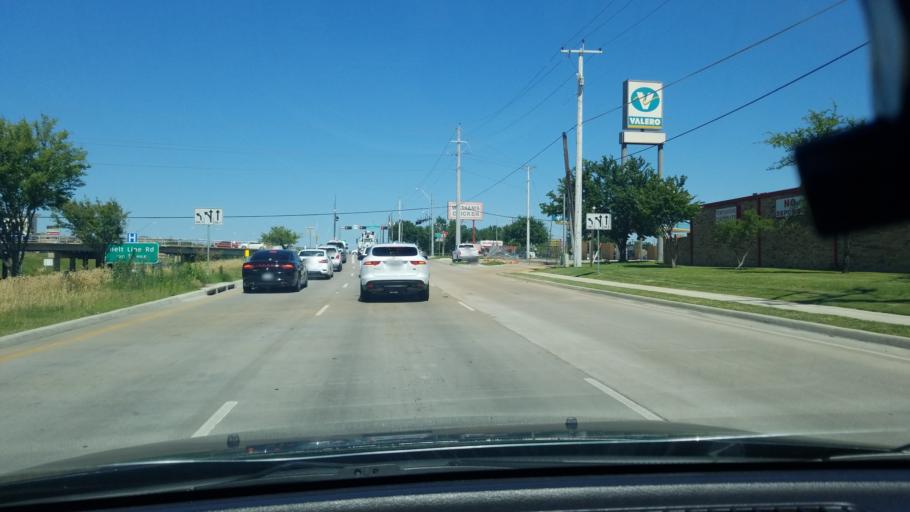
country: US
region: Texas
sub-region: Dallas County
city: Mesquite
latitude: 32.7922
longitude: -96.6134
